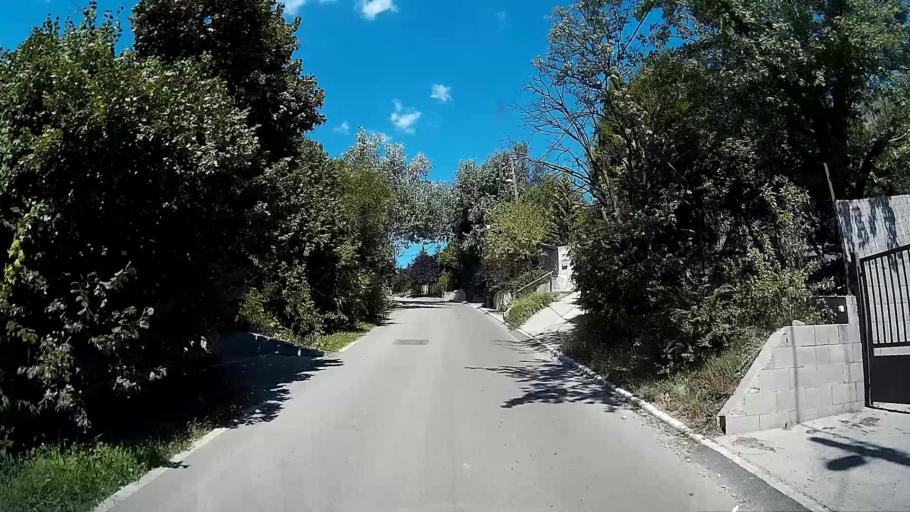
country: HU
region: Pest
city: Leanyfalu
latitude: 47.6934
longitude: 19.0838
